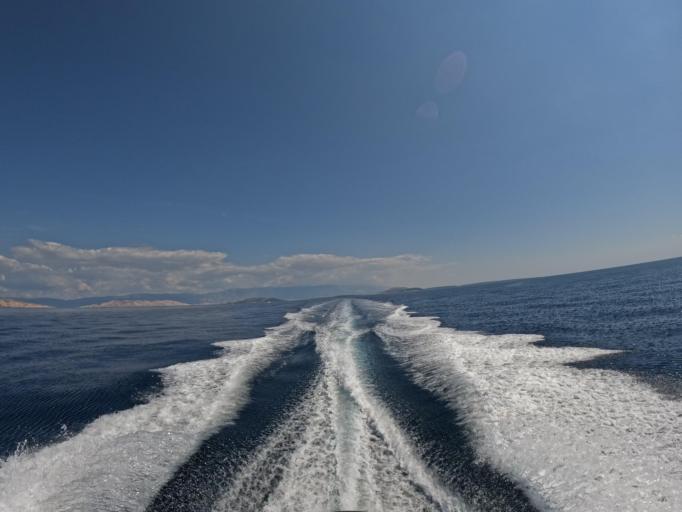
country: HR
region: Primorsko-Goranska
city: Punat
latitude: 44.9055
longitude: 14.6022
